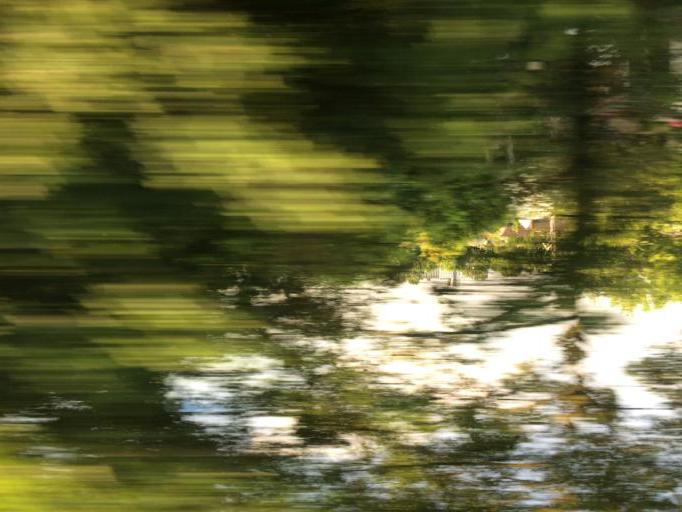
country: DE
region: North Rhine-Westphalia
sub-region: Regierungsbezirk Dusseldorf
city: Muelheim (Ruhr)
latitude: 51.4491
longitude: 6.8335
